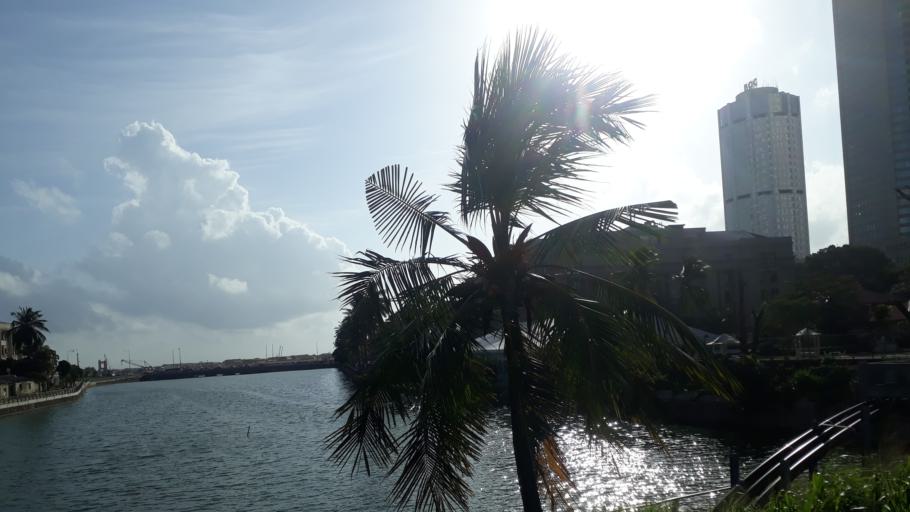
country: LK
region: Western
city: Colombo
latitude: 6.9304
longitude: 79.8462
